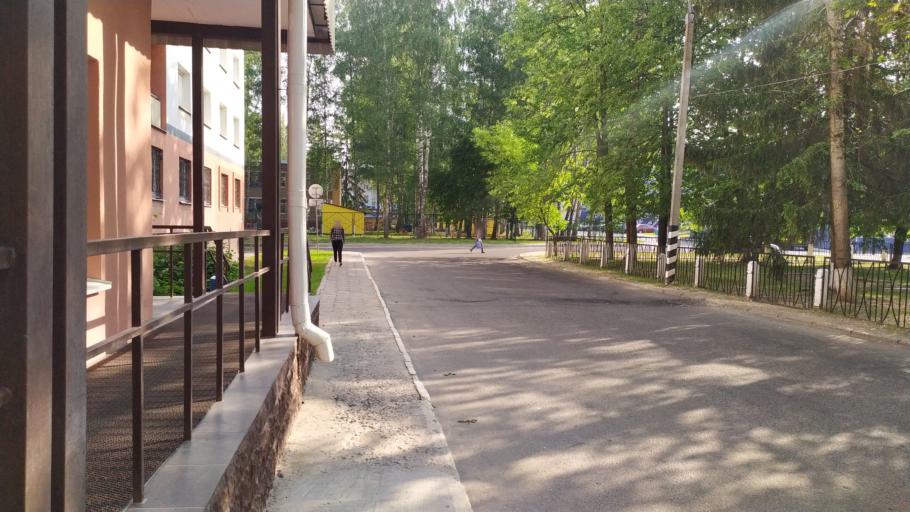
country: BY
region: Vitebsk
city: Navapolatsk
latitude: 55.5312
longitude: 28.6496
